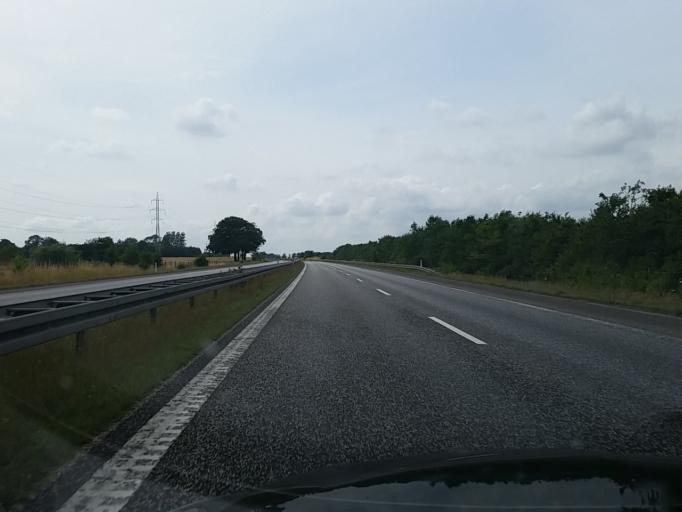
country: DK
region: South Denmark
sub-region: Kolding Kommune
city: Lunderskov
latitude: 55.5074
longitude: 9.3176
